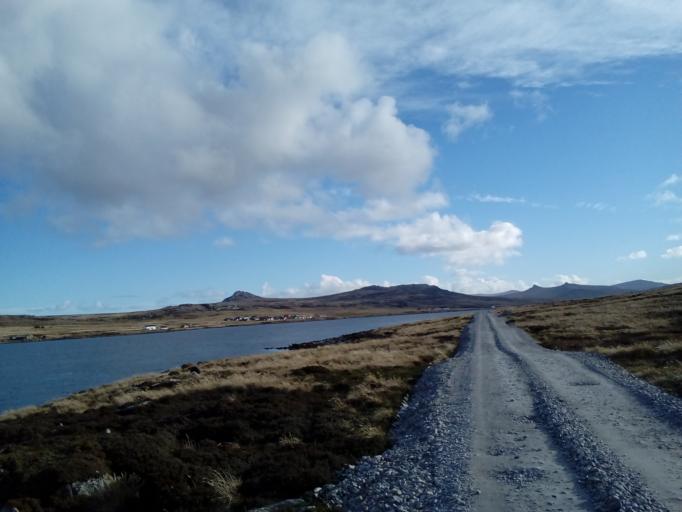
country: FK
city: Stanley
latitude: -51.6839
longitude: -57.8908
